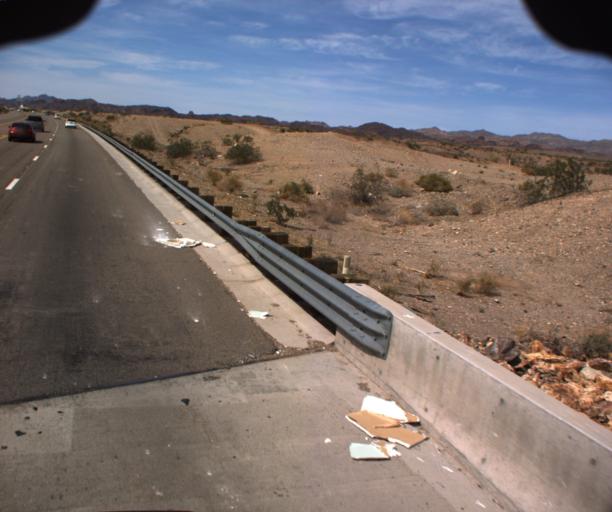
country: US
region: Arizona
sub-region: Mohave County
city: Desert Hills
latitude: 34.5285
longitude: -114.3496
